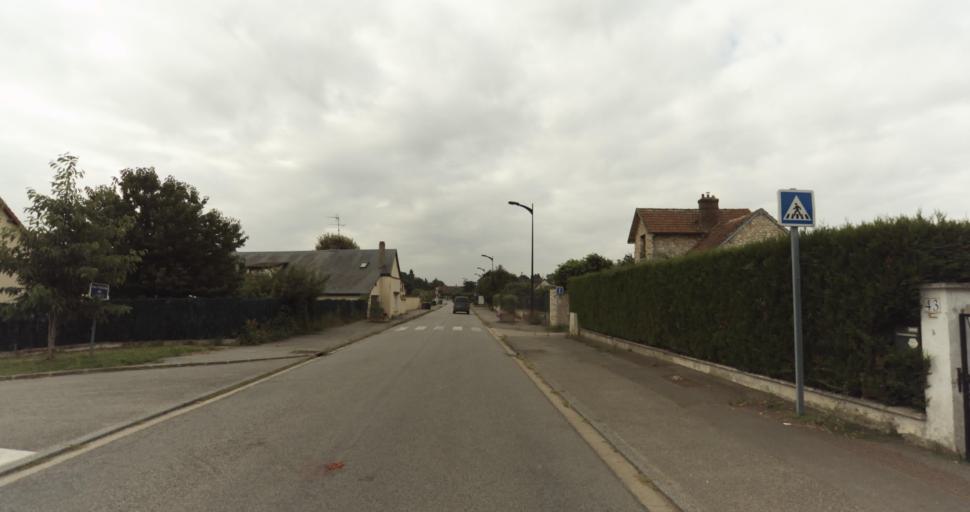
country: FR
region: Haute-Normandie
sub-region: Departement de l'Eure
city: Marcilly-sur-Eure
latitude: 48.8293
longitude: 1.3478
